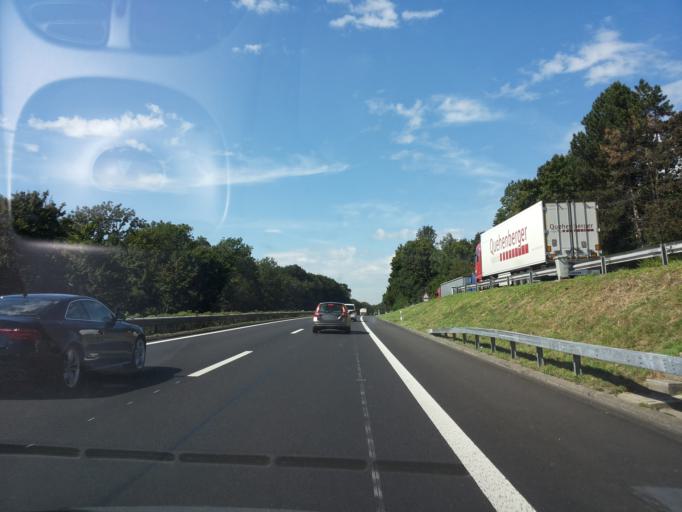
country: CH
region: Lucerne
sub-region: Sursee District
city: Sempach
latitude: 47.1442
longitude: 8.1839
